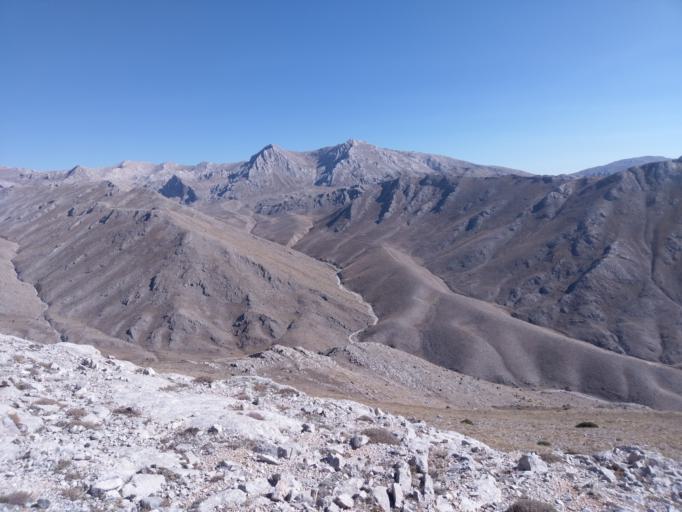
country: TR
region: Kayseri
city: Toklar
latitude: 38.4397
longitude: 36.1681
